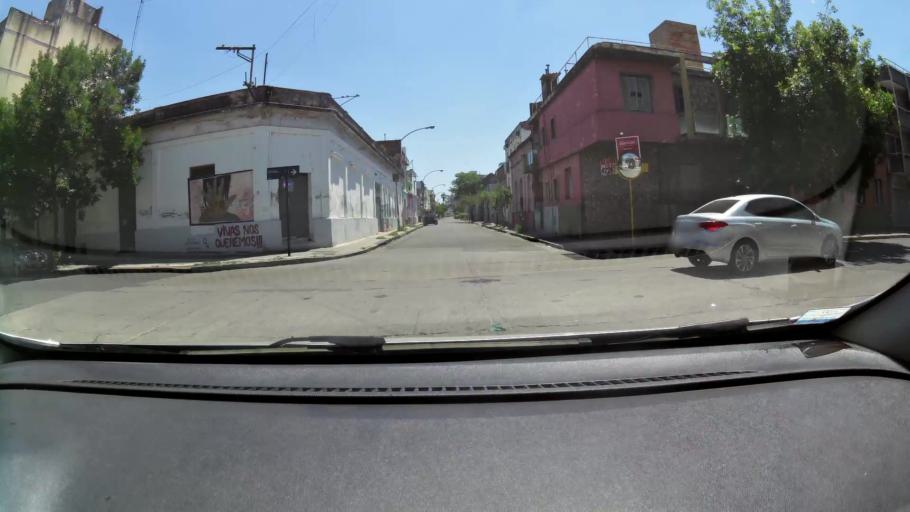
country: AR
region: Cordoba
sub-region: Departamento de Capital
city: Cordoba
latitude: -31.4074
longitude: -64.1788
